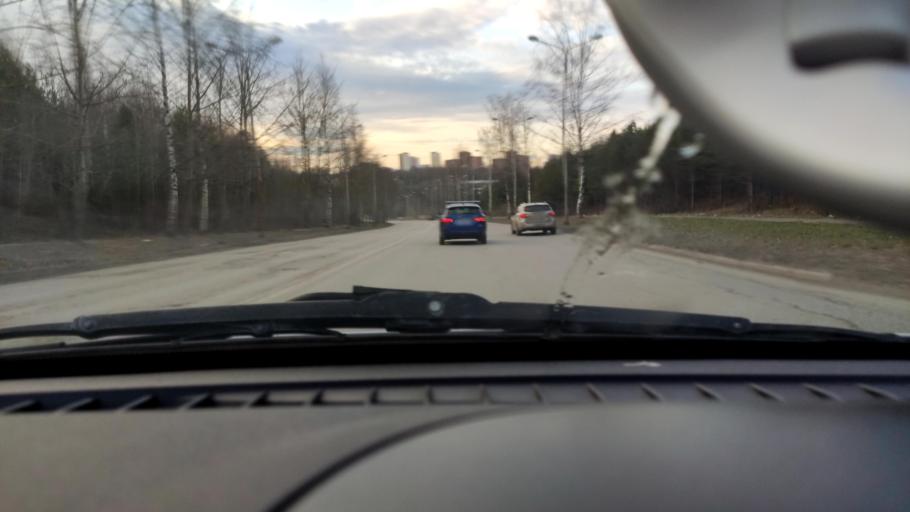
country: RU
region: Perm
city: Perm
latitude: 58.0755
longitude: 56.3694
